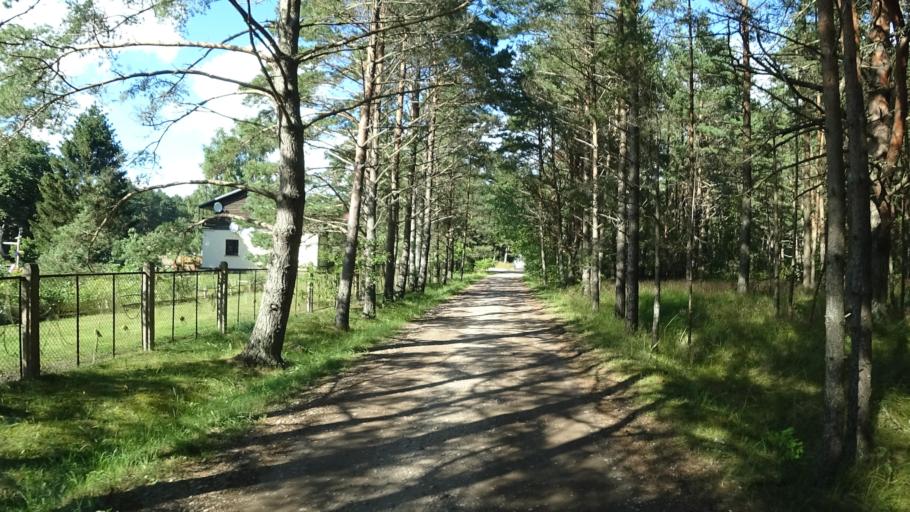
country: LV
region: Ventspils
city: Ventspils
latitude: 57.4885
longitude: 21.6481
